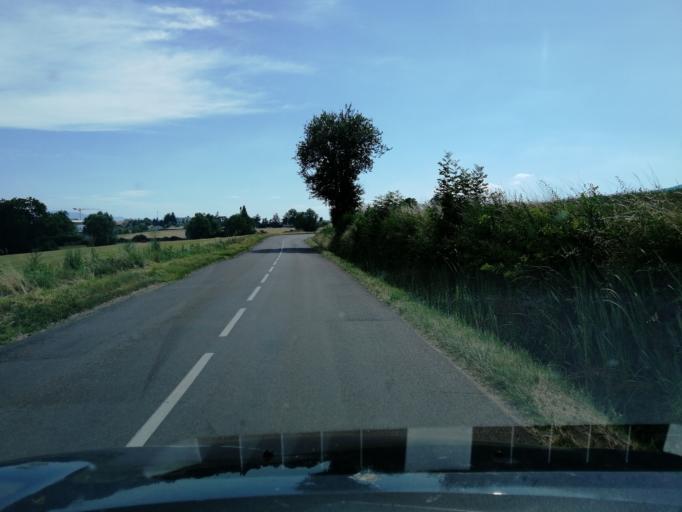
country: FR
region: Rhone-Alpes
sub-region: Departement du Rhone
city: Mornant
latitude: 45.6308
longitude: 4.6752
